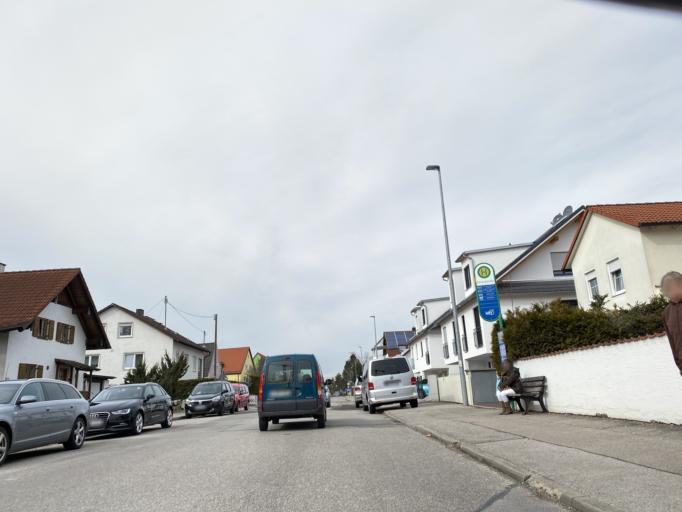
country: DE
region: Bavaria
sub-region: Upper Bavaria
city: Fuerstenfeldbruck
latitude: 48.1773
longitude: 11.2389
